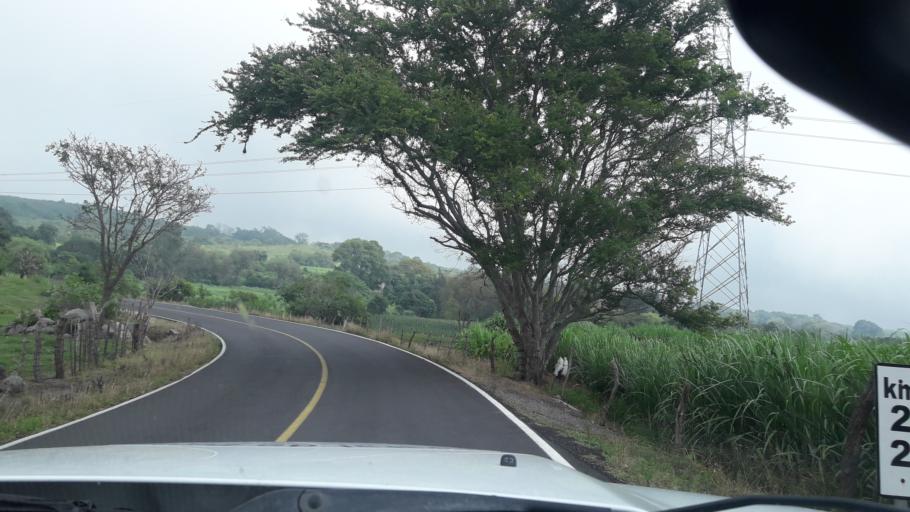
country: MX
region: Colima
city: Queseria
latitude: 19.4091
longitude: -103.6410
